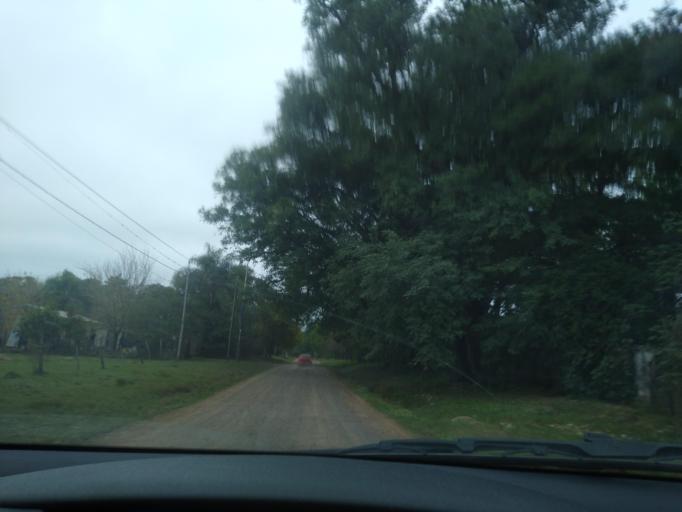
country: AR
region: Chaco
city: Colonia Benitez
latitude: -27.3350
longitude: -58.9562
